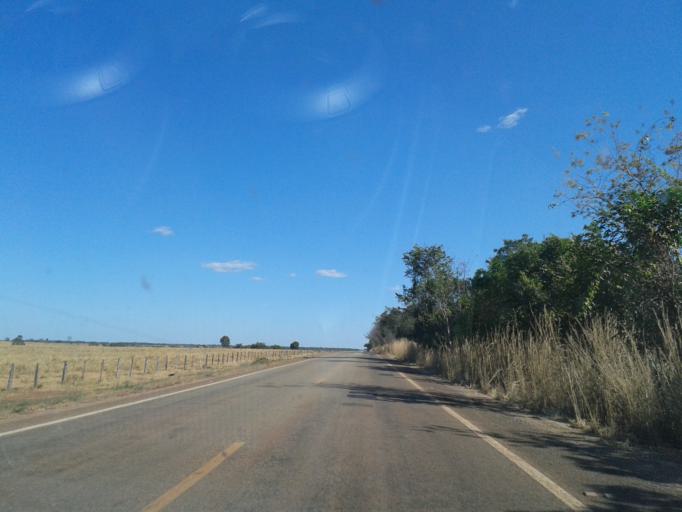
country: BR
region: Goias
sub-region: Mozarlandia
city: Mozarlandia
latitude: -14.3890
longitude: -50.4380
